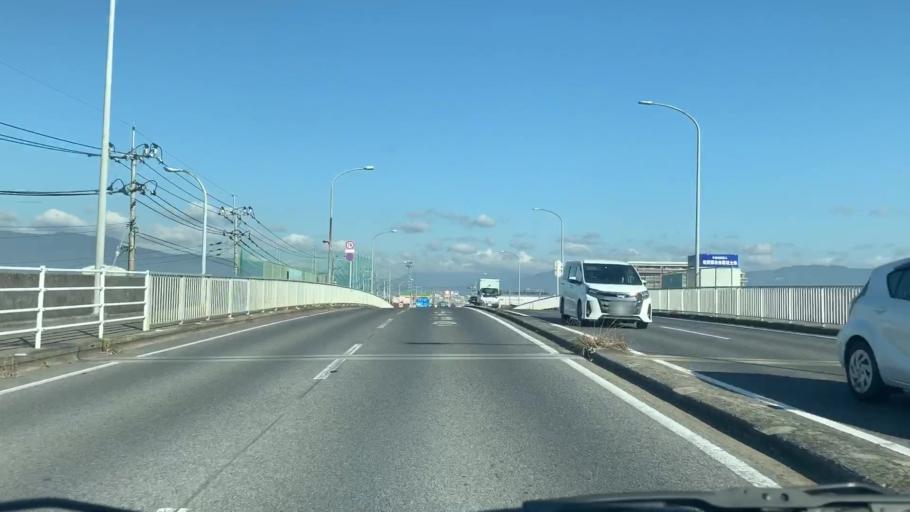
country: JP
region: Saga Prefecture
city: Saga-shi
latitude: 33.2591
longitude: 130.2731
